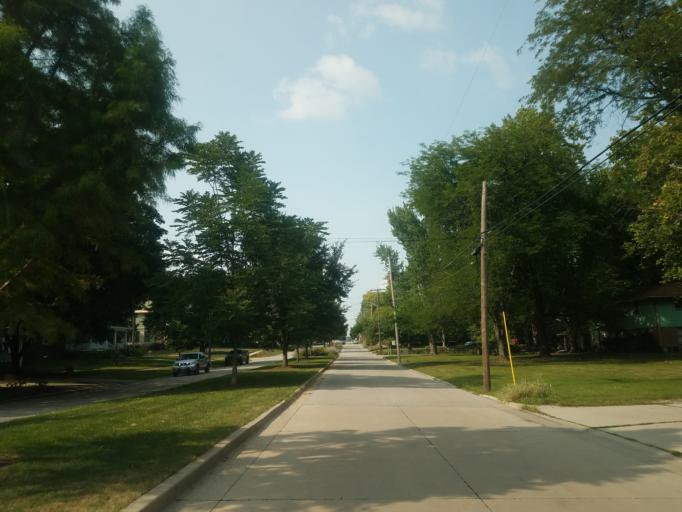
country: US
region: Illinois
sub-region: McLean County
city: Normal
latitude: 40.5032
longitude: -88.9856
